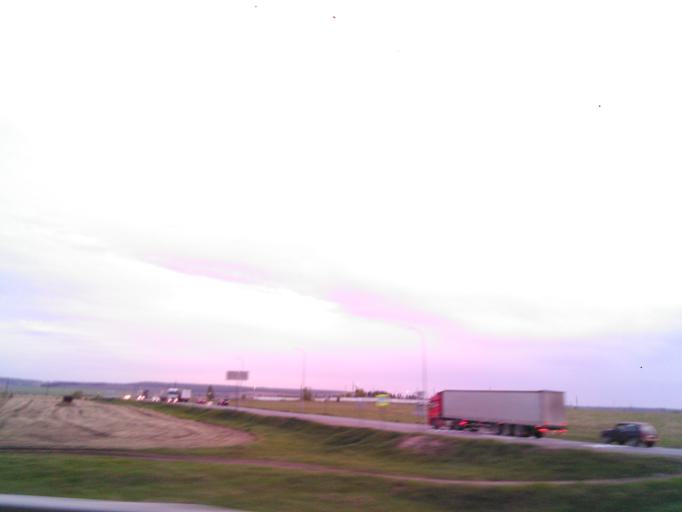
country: RU
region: Tatarstan
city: Russkiy Aktash
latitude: 55.0473
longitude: 52.1002
